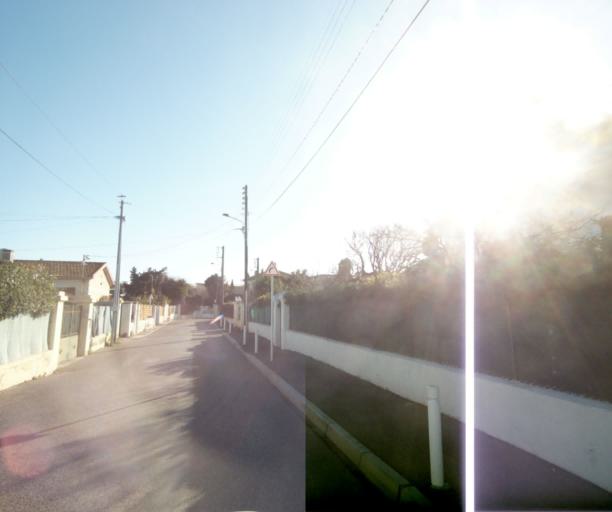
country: FR
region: Provence-Alpes-Cote d'Azur
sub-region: Departement des Alpes-Maritimes
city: Antibes
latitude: 43.5959
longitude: 7.1242
